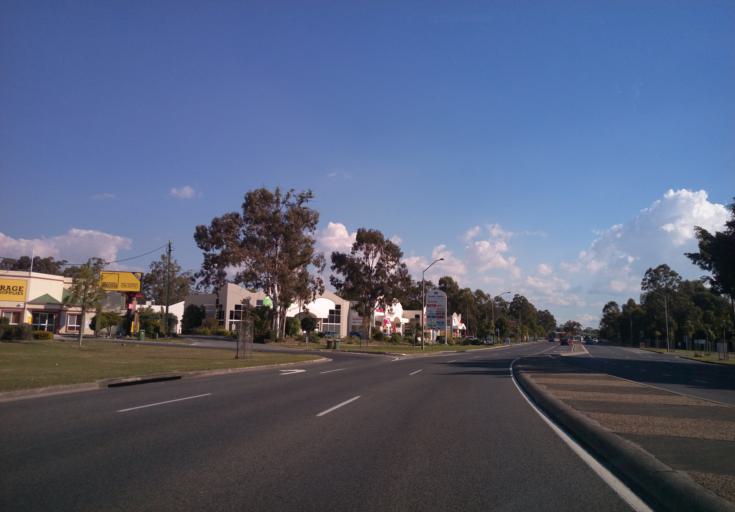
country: AU
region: Queensland
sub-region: Brisbane
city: Chandler
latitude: -27.5227
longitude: 153.1999
